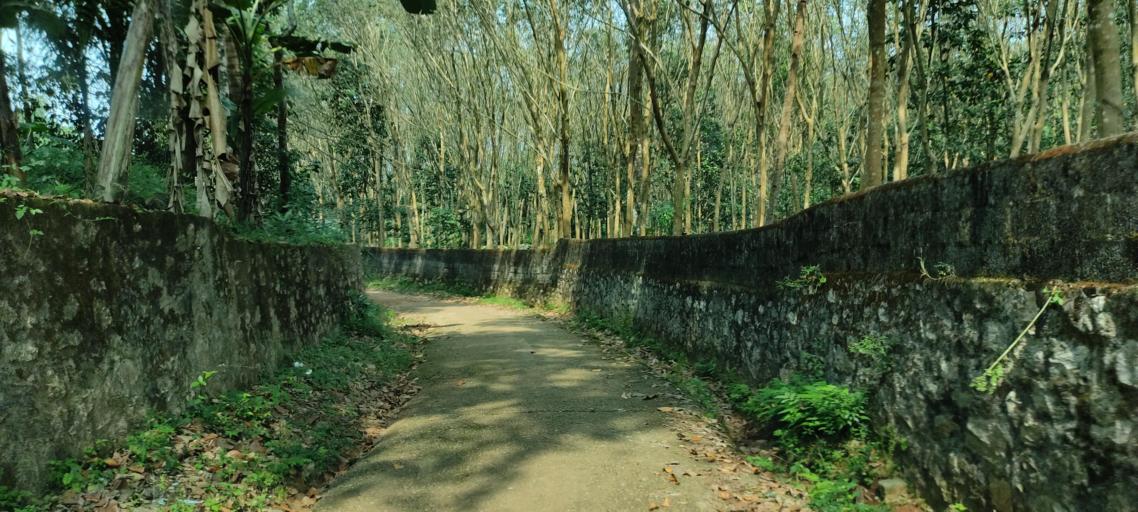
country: IN
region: Kerala
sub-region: Pattanamtitta
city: Adur
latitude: 9.2139
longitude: 76.6945
